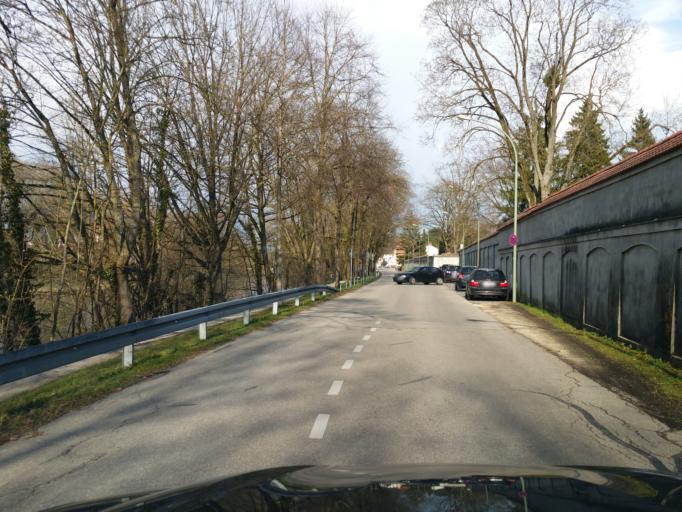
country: DE
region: Bavaria
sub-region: Lower Bavaria
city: Landshut
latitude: 48.5422
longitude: 12.1609
